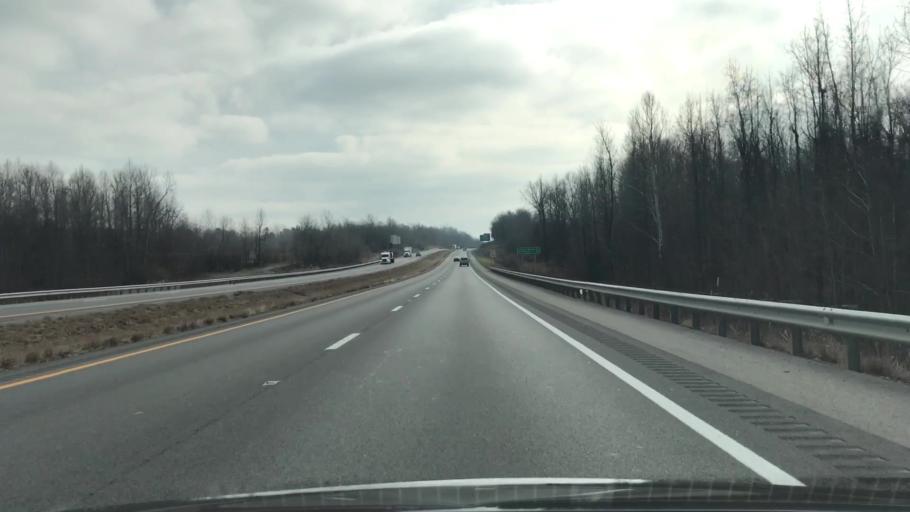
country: US
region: Kentucky
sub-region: Hopkins County
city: Earlington
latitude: 37.2888
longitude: -87.4597
